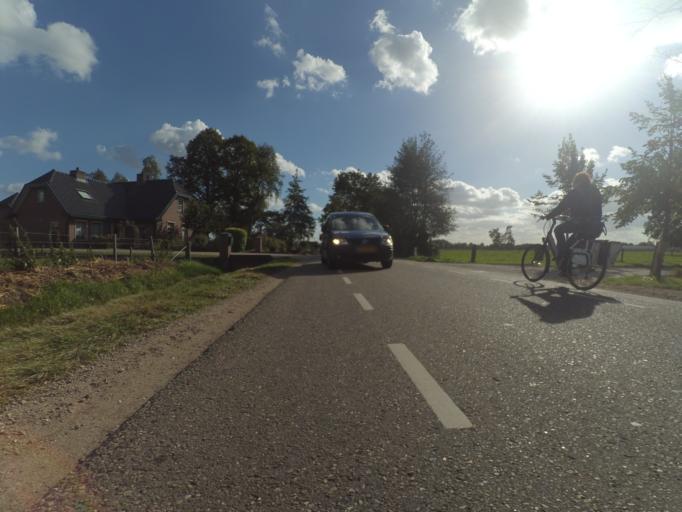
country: NL
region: Gelderland
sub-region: Gemeente Ede
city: Ederveen
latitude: 52.0580
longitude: 5.6067
